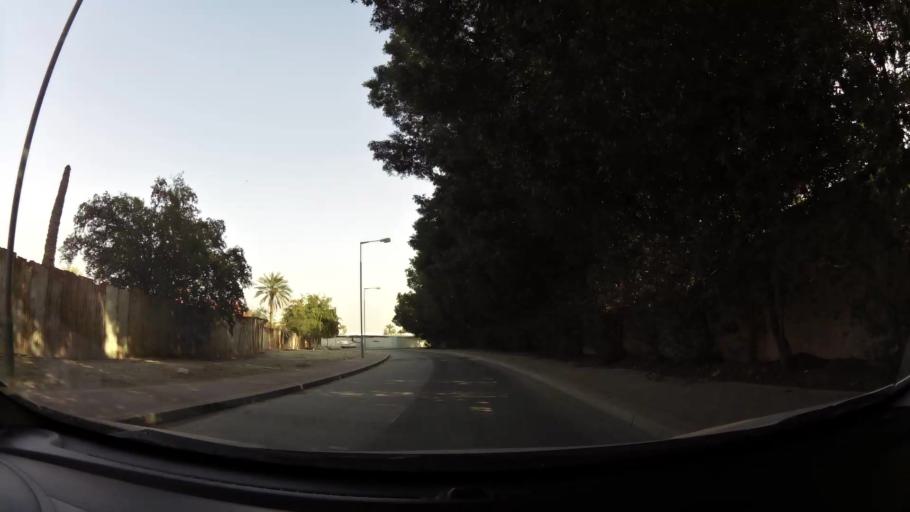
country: BH
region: Manama
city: Jidd Hafs
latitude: 26.2126
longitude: 50.5114
